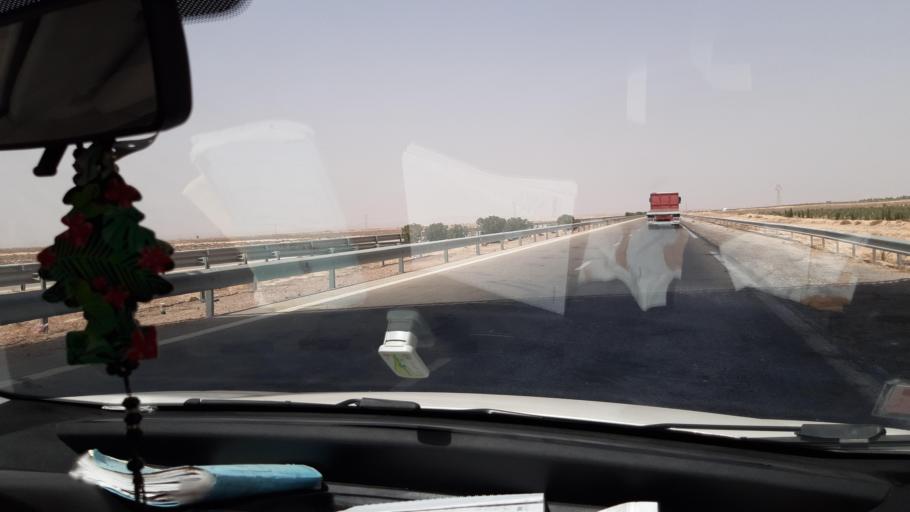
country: TN
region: Qabis
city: Gabes
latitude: 33.9344
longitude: 9.9633
